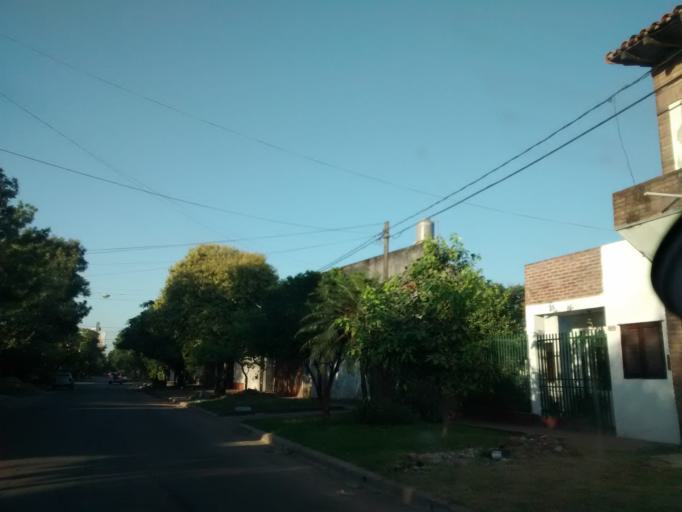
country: AR
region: Chaco
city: Resistencia
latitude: -27.4487
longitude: -58.9716
